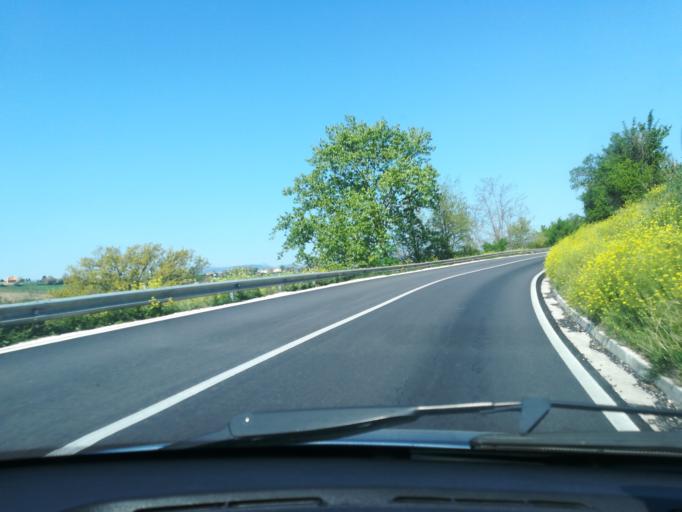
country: IT
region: The Marches
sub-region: Provincia di Macerata
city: Villa Potenza
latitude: 43.3290
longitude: 13.3890
